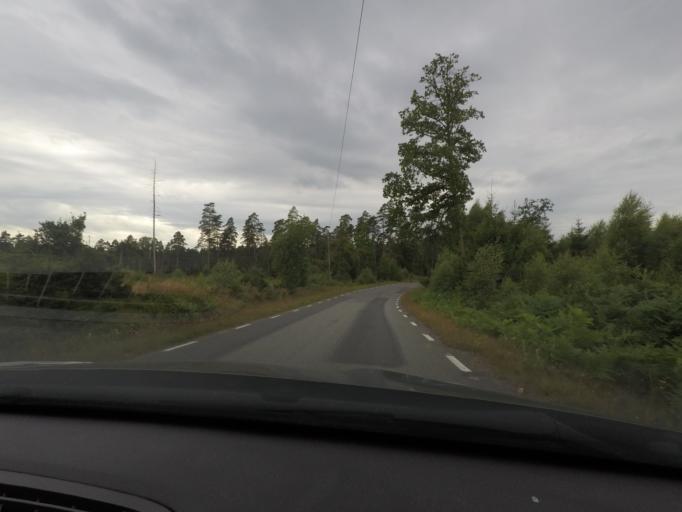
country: SE
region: Kronoberg
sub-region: Markaryds Kommun
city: Markaryd
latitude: 56.4155
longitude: 13.7004
